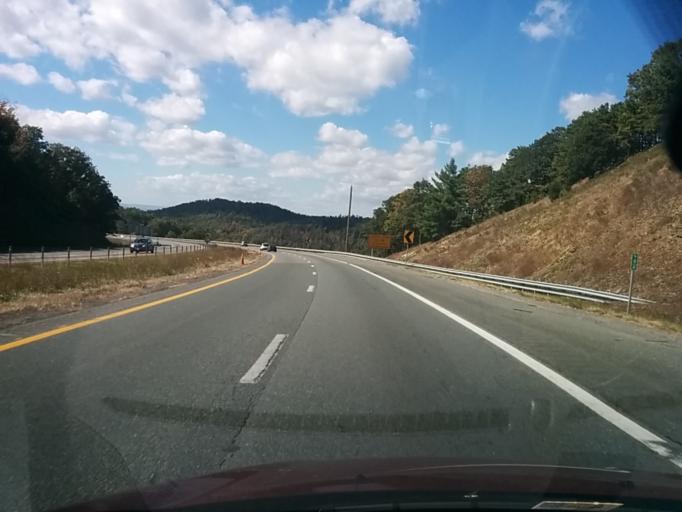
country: US
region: Virginia
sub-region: City of Waynesboro
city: Waynesboro
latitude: 38.0409
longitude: -78.8738
